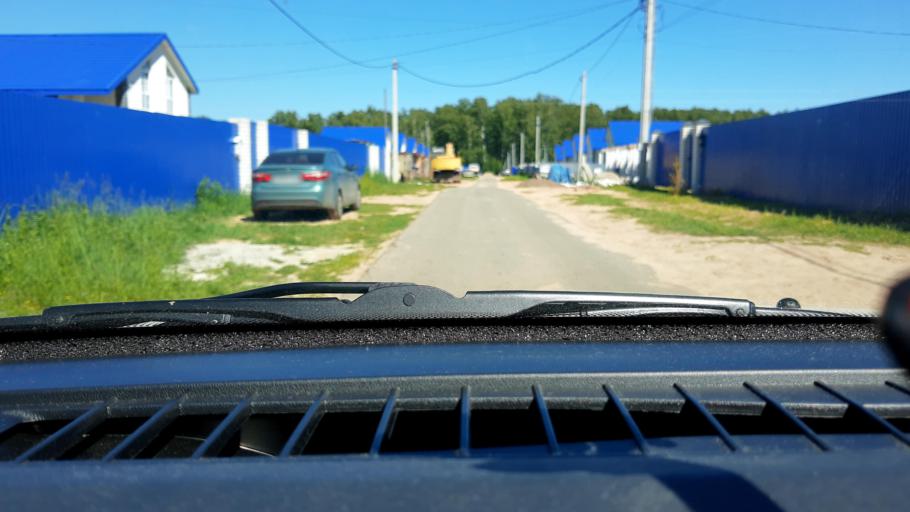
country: RU
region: Nizjnij Novgorod
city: Neklyudovo
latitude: 56.4098
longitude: 44.0257
